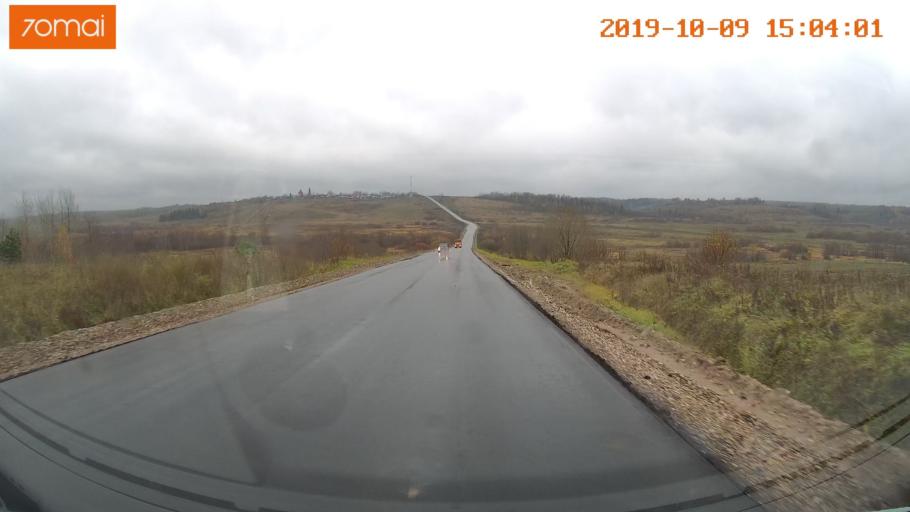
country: RU
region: Kostroma
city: Chistyye Bory
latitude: 58.2638
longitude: 41.6710
